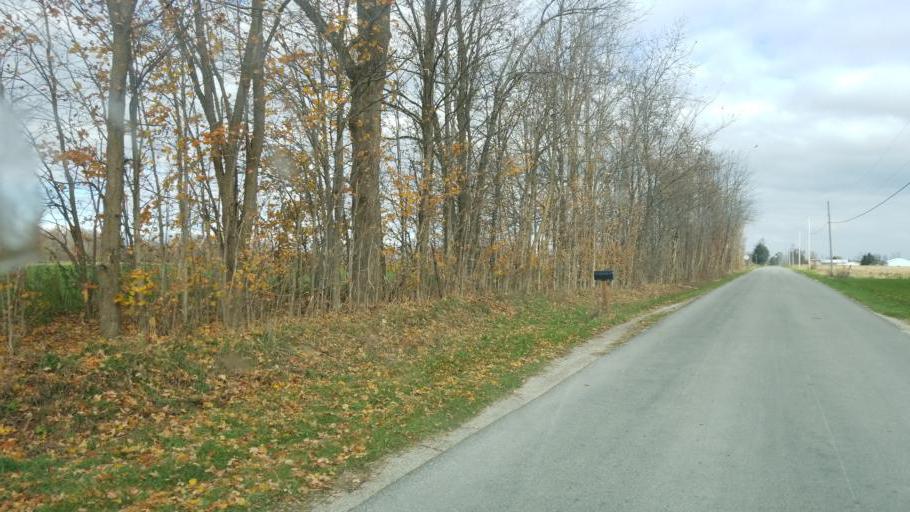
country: US
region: Ohio
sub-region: Crawford County
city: Galion
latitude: 40.6541
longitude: -82.7846
